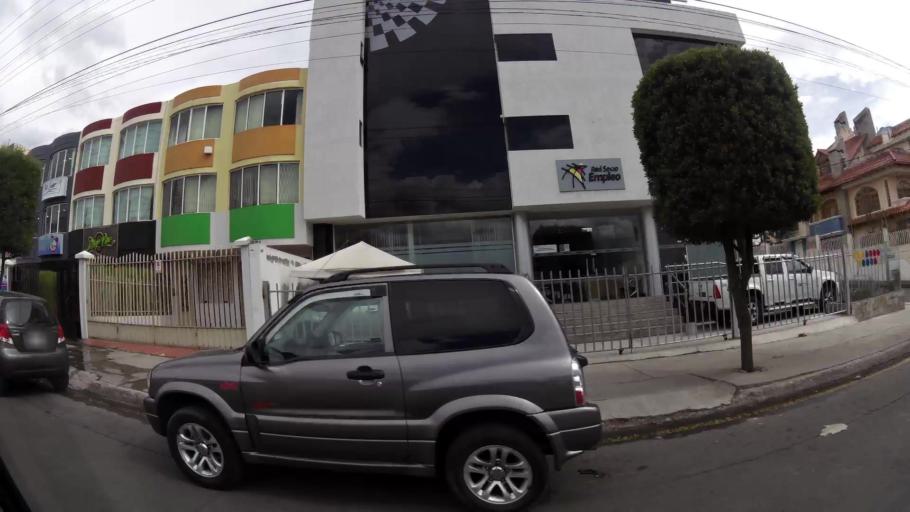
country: EC
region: Tungurahua
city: Ambato
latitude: -1.2678
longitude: -78.6331
